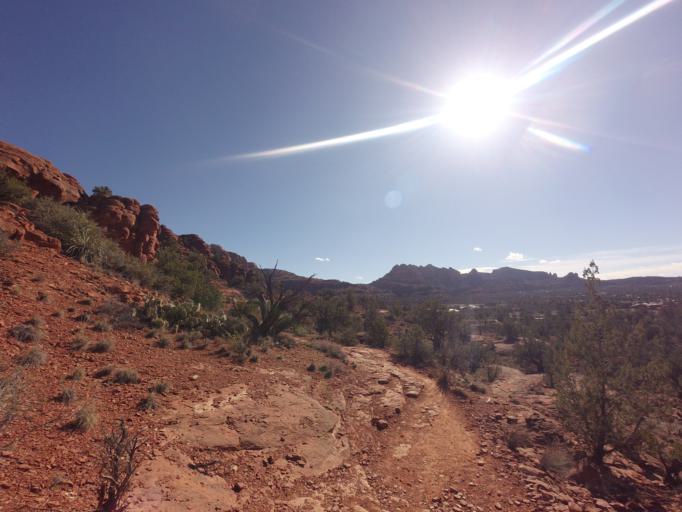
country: US
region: Arizona
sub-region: Yavapai County
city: West Sedona
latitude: 34.8141
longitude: -111.8056
